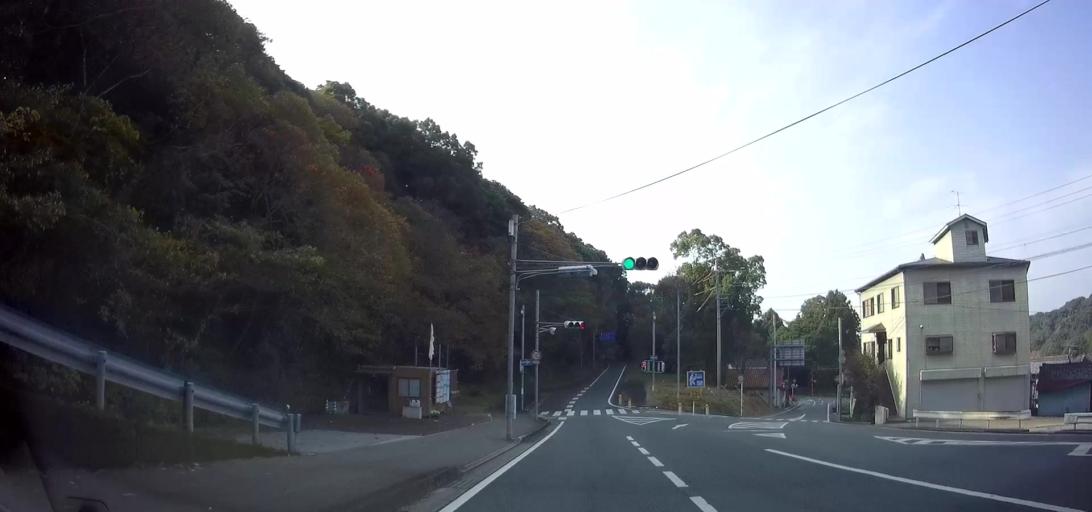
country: JP
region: Nagasaki
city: Shimabara
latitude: 32.6855
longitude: 130.2014
